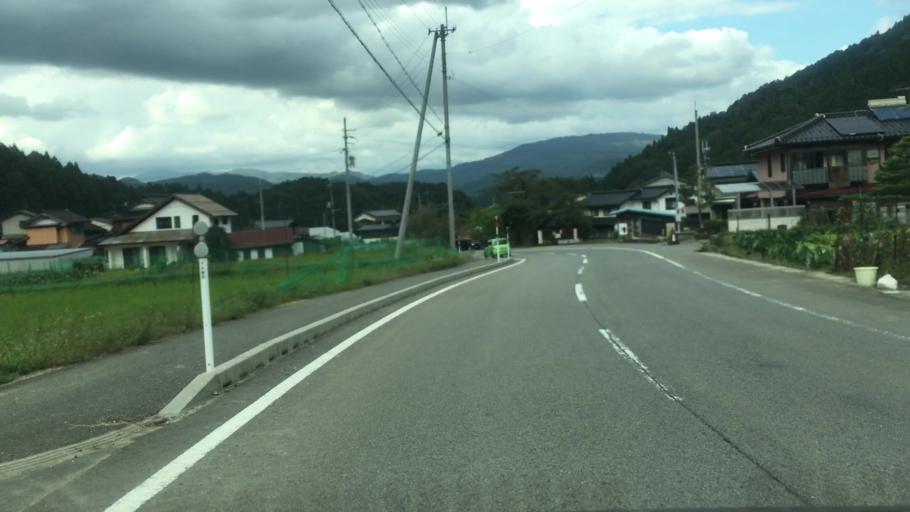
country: JP
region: Hyogo
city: Toyooka
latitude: 35.4385
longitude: 134.7333
